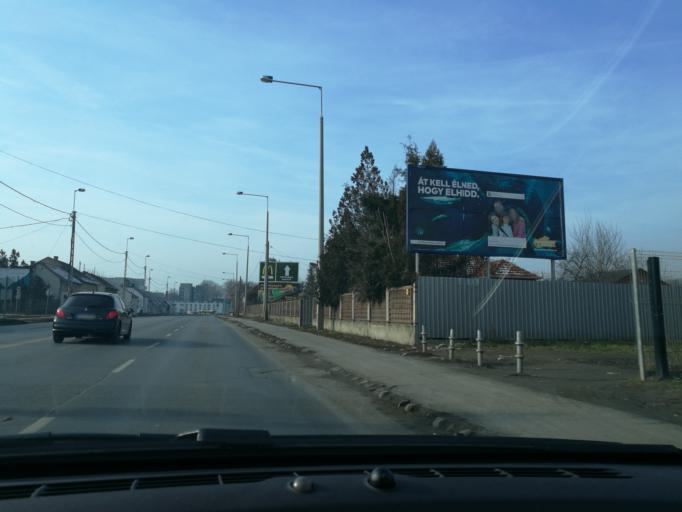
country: HU
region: Szabolcs-Szatmar-Bereg
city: Nyiregyhaza
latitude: 47.9521
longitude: 21.7384
